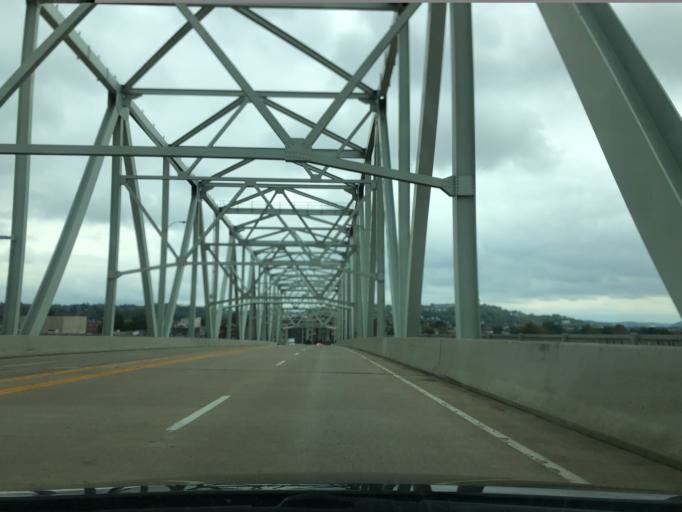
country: US
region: Kentucky
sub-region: Campbell County
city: Newport
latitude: 39.0960
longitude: -84.5012
